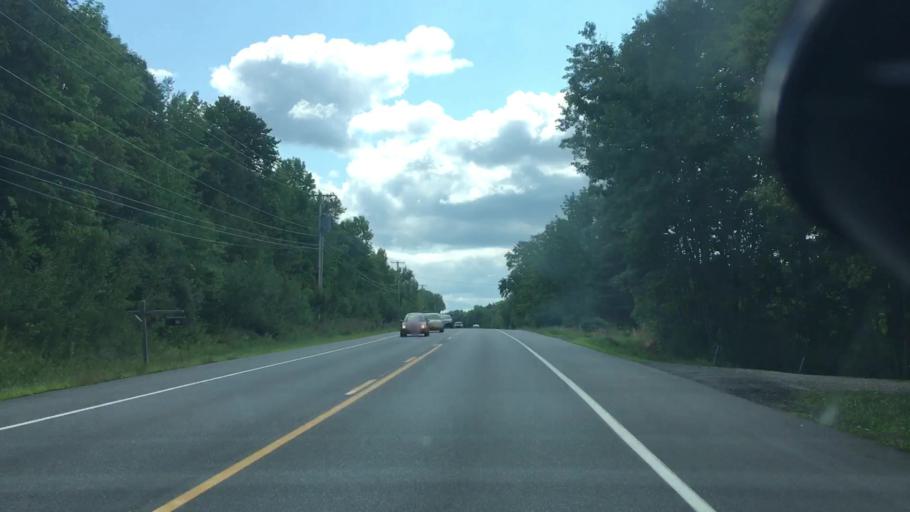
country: US
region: Maine
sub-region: Kennebec County
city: Waterville
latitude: 44.5894
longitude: -69.6523
